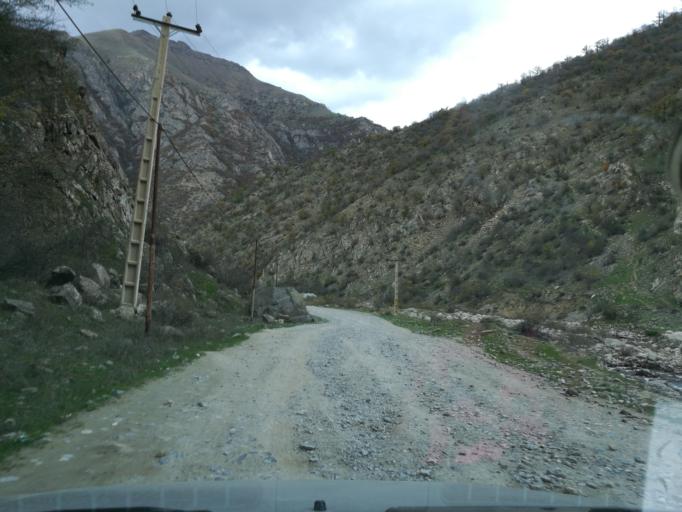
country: IR
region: Mazandaran
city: `Abbasabad
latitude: 36.4393
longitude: 51.0675
